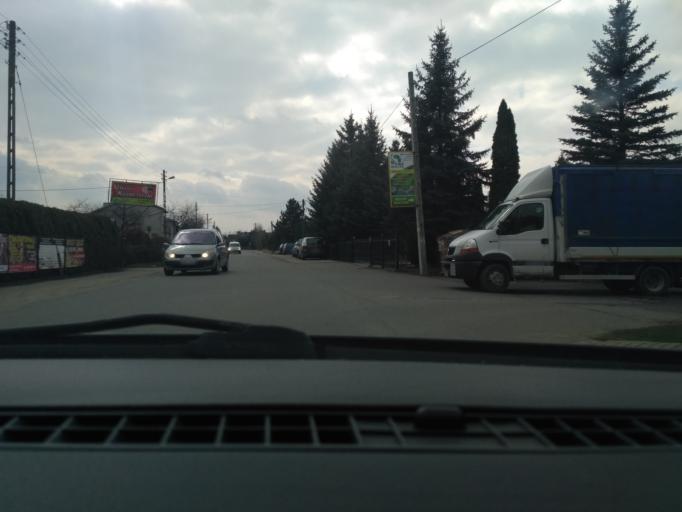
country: PL
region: Subcarpathian Voivodeship
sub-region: Powiat krosnienski
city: Kroscienko Wyzne
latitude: 49.6647
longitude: 21.8312
